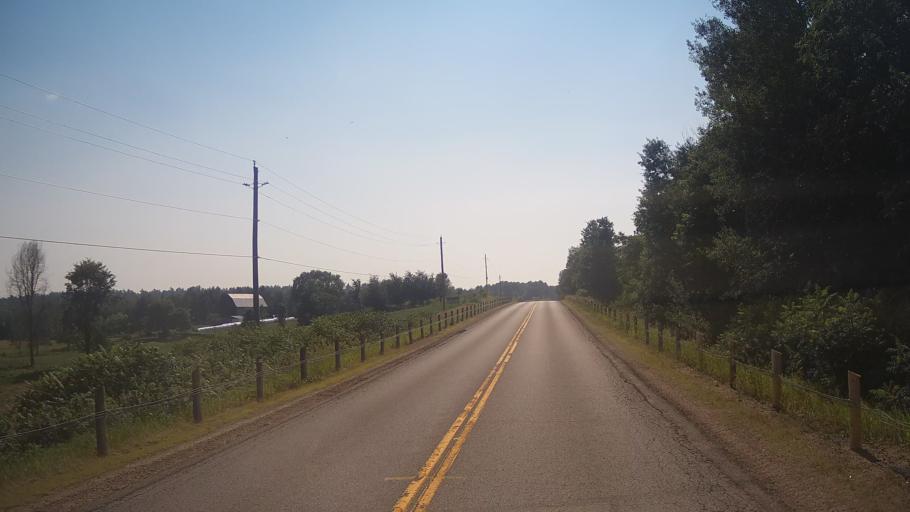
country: CA
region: Ontario
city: Pembroke
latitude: 45.6113
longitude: -77.2002
